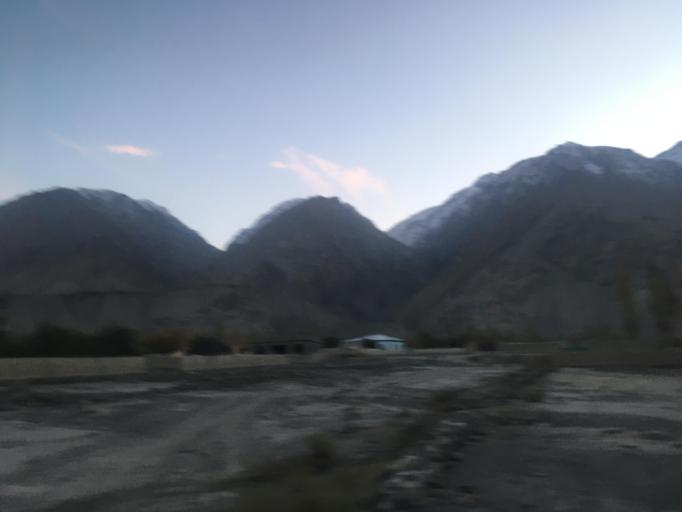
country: PK
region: Gilgit-Baltistan
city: Skardu
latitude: 35.3003
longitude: 75.5438
